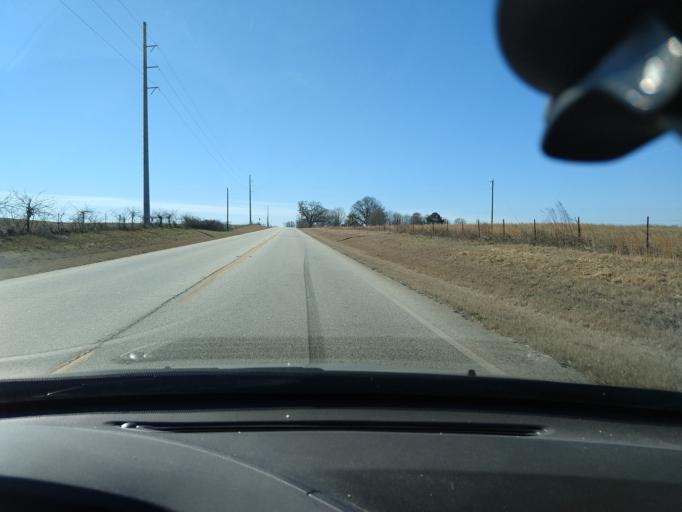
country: US
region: Georgia
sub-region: Newton County
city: Covington
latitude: 33.4939
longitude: -83.7385
